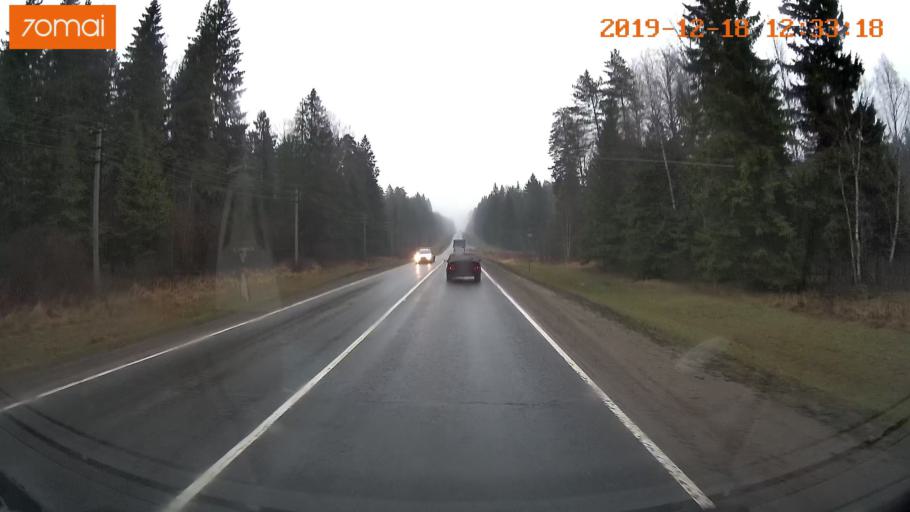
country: RU
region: Moskovskaya
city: Rumyantsevo
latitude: 56.1115
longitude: 36.5592
